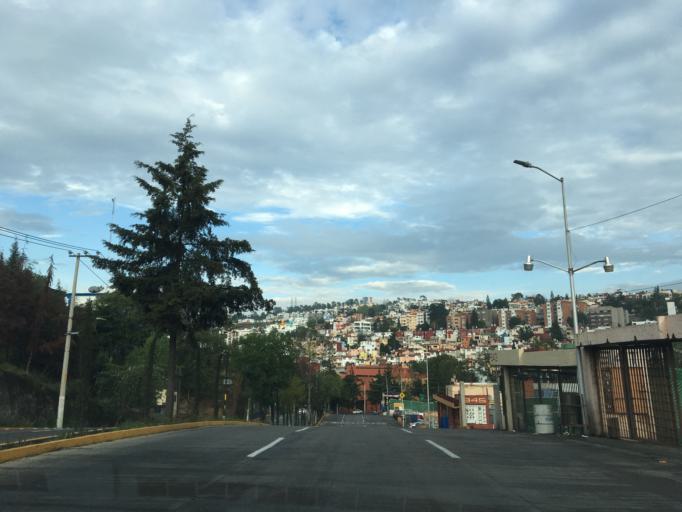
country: MX
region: Mexico
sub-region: Naucalpan de Juarez
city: Rincon Verde
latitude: 19.5176
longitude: -99.2695
